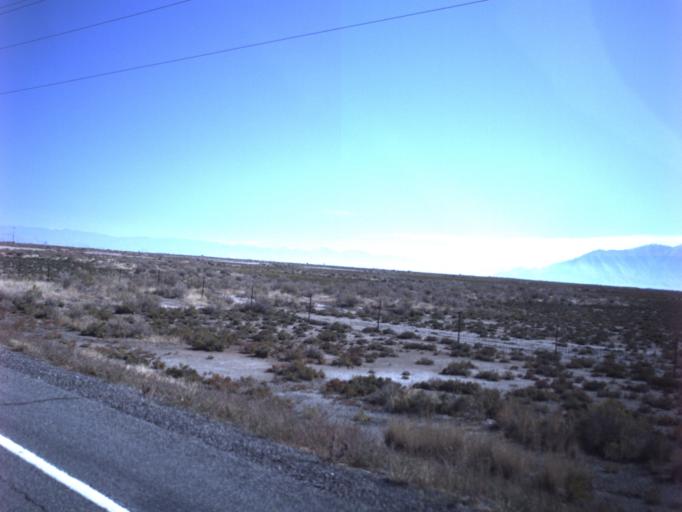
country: US
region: Utah
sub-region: Tooele County
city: Grantsville
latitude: 40.6959
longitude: -112.5310
